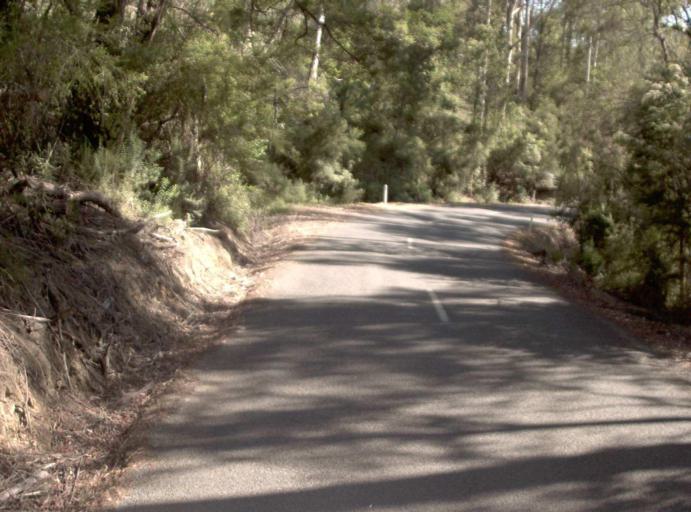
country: AU
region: Victoria
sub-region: East Gippsland
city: Lakes Entrance
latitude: -37.5036
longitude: 148.5421
